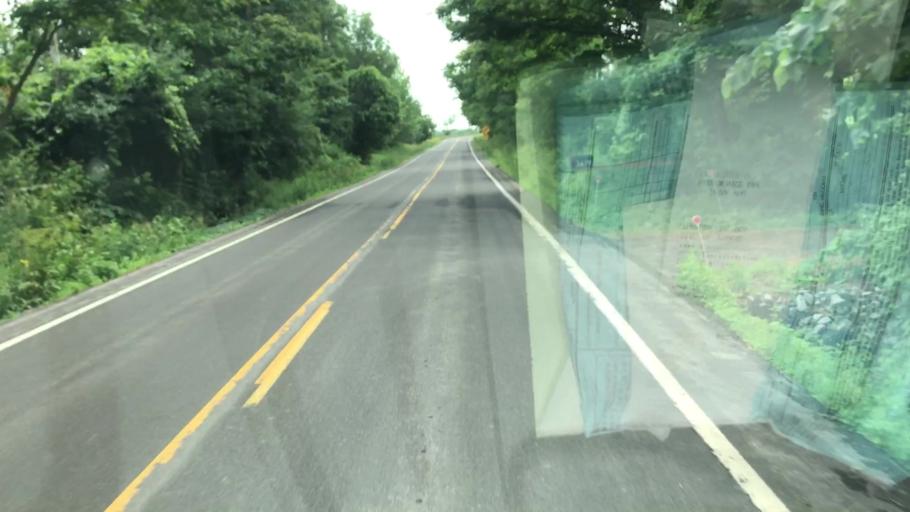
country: US
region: New York
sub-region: Onondaga County
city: Manlius
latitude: 42.9402
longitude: -75.9781
